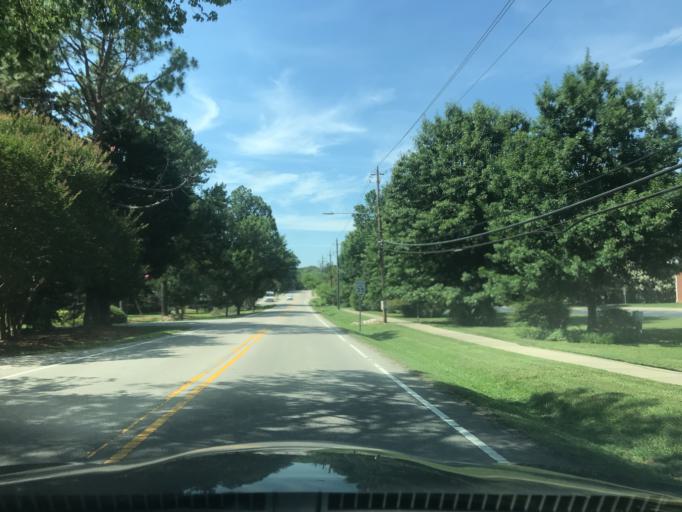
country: US
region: North Carolina
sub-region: Wake County
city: Wendell
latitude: 35.7785
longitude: -78.3621
